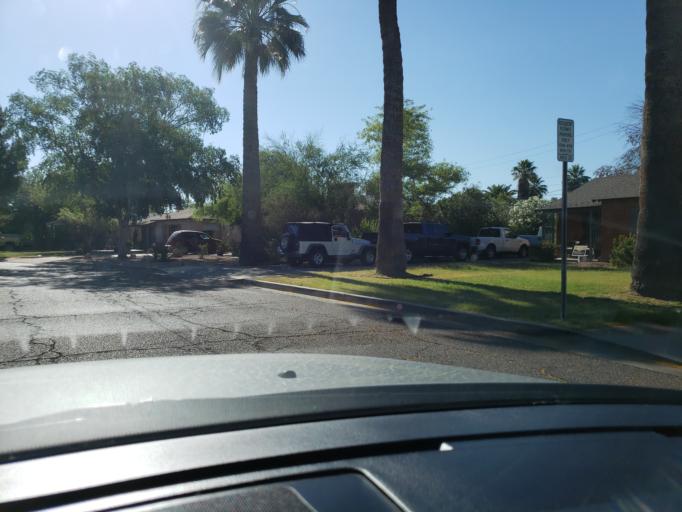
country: US
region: Arizona
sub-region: Maricopa County
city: Phoenix
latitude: 33.4781
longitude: -112.0620
